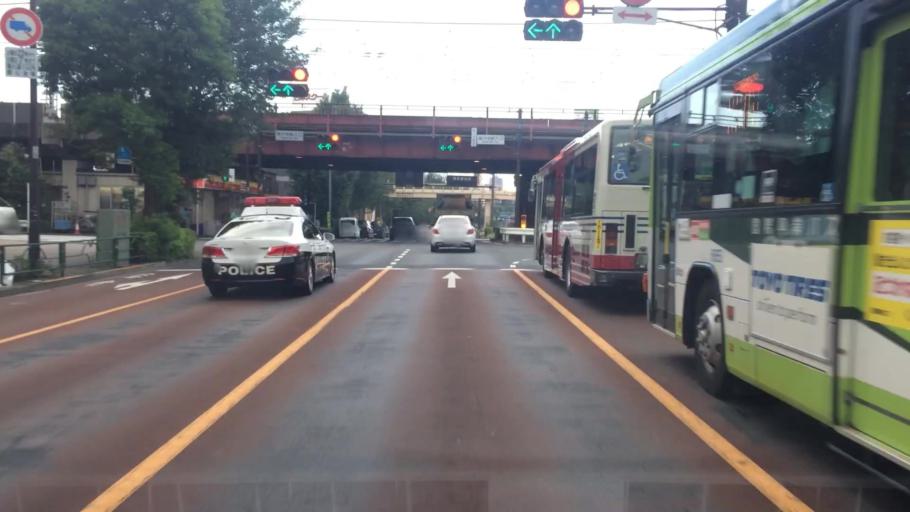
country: JP
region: Tokyo
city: Tokyo
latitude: 35.7059
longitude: 139.6546
